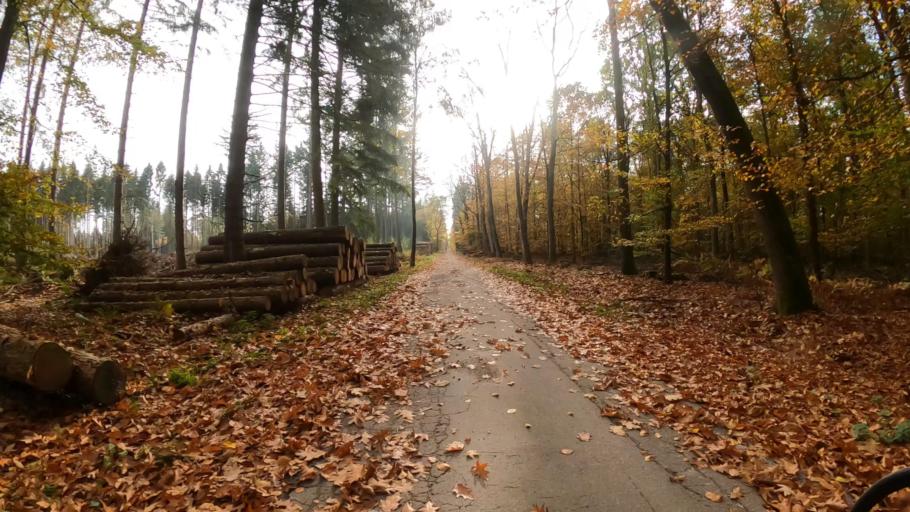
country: DE
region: Lower Saxony
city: Buchholz in der Nordheide
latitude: 53.3587
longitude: 9.8228
